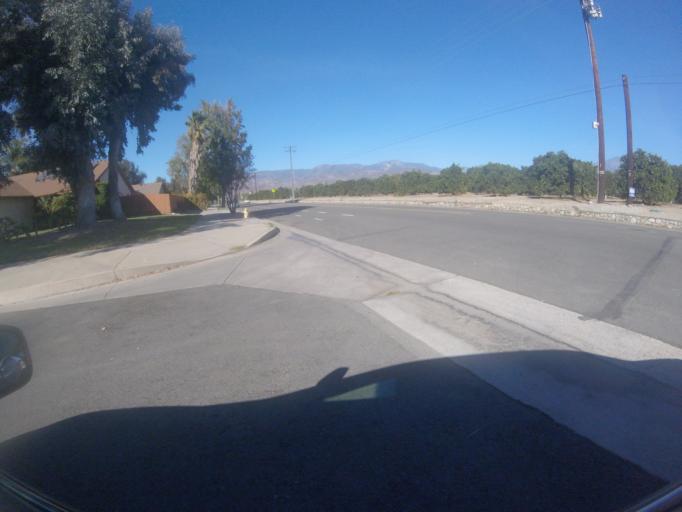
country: US
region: California
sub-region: San Bernardino County
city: Mentone
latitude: 34.0714
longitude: -117.1565
